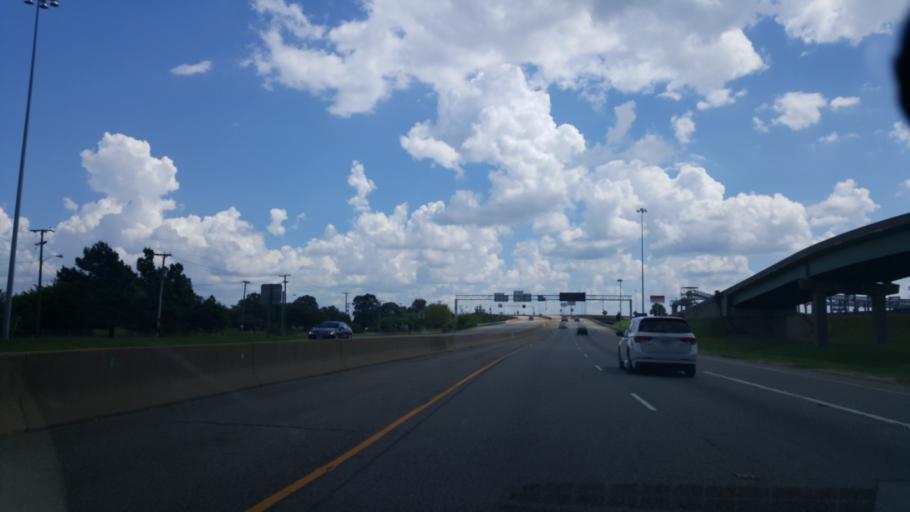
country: US
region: Virginia
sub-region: City of Newport News
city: Newport News
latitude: 36.9800
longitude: -76.4241
